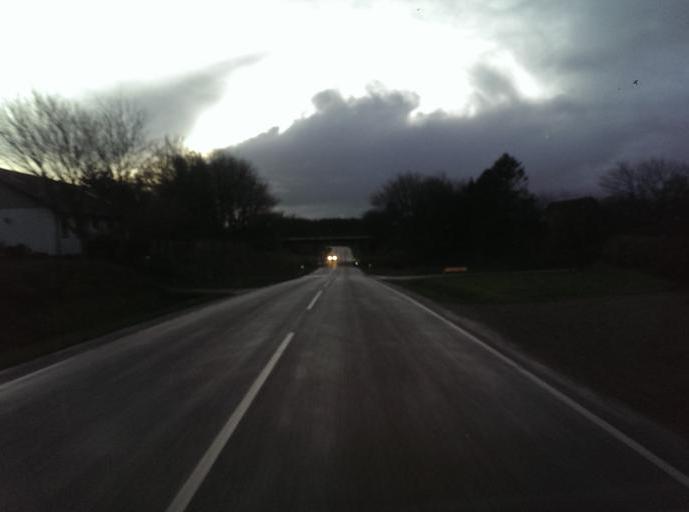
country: DK
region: South Denmark
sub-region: Esbjerg Kommune
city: Bramming
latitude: 55.4301
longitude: 8.6703
